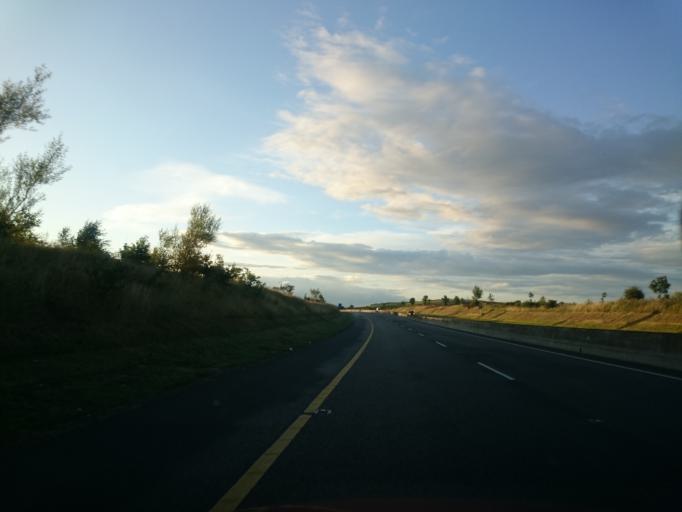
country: IE
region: Leinster
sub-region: Loch Garman
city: Gorey
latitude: 52.6757
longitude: -6.2577
